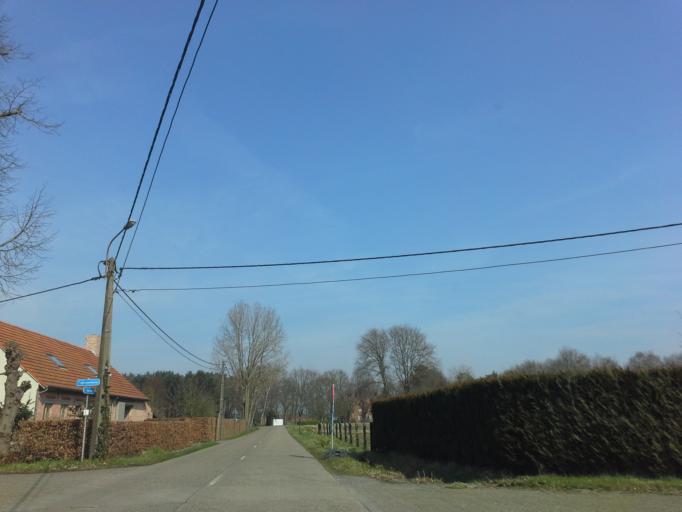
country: BE
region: Flanders
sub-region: Provincie Antwerpen
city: Meerhout
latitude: 51.1301
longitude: 5.0520
